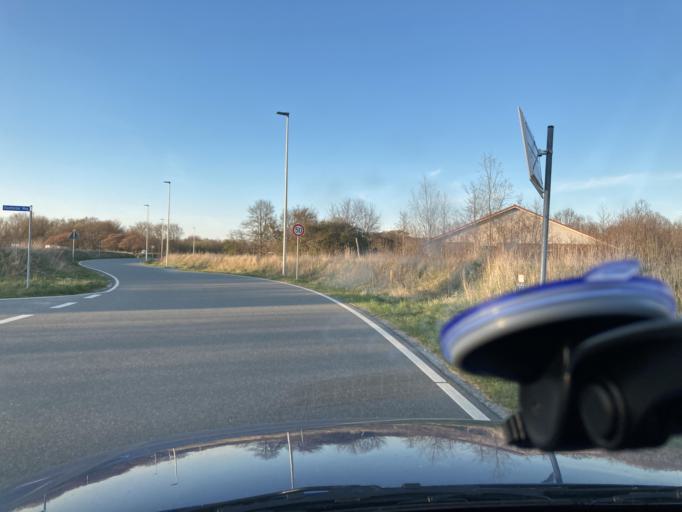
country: DE
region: Schleswig-Holstein
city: Lohe-Rickelshof
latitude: 54.1976
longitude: 9.0734
